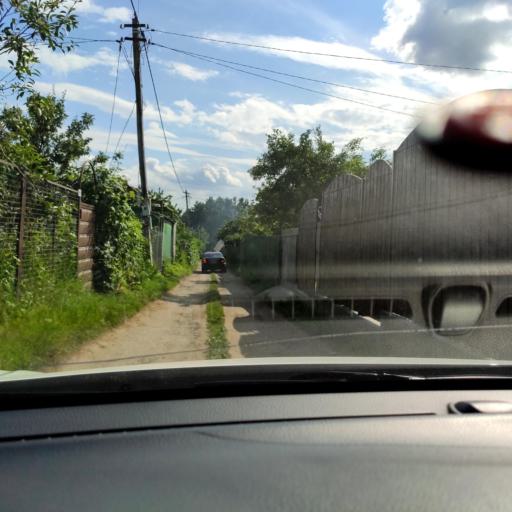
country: RU
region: Tatarstan
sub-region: Gorod Kazan'
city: Kazan
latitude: 55.8896
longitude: 49.0580
